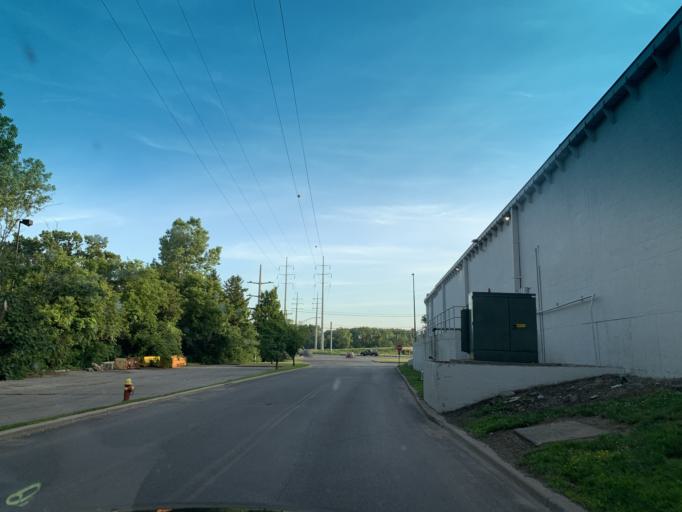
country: US
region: New York
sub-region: Oneida County
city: Utica
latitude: 43.1229
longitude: -75.2251
